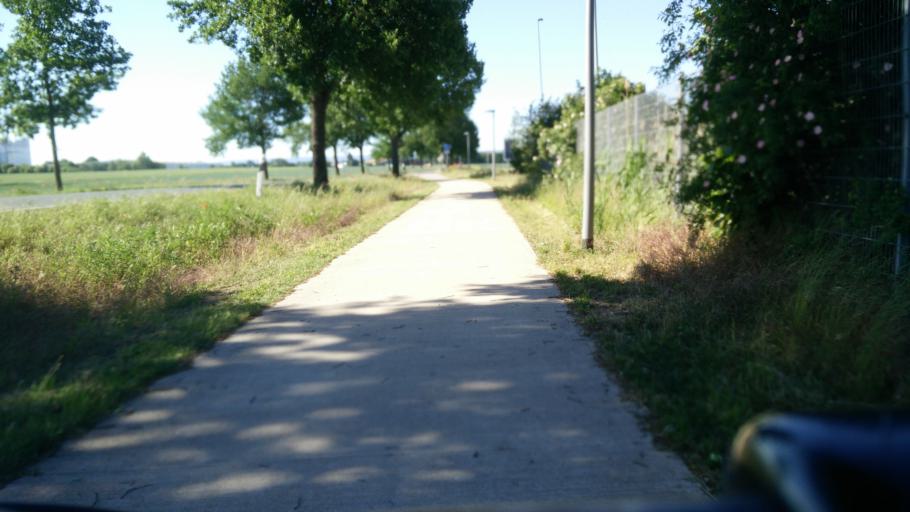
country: DE
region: Lower Saxony
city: Wunstorf
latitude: 52.4089
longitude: 9.4649
